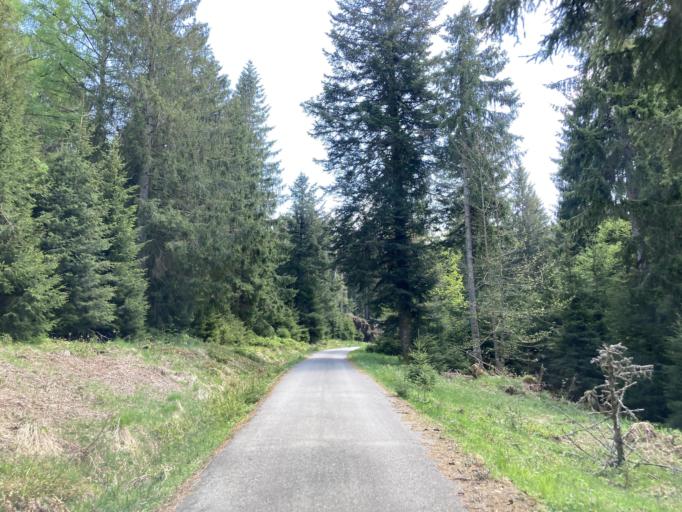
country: DE
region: Baden-Wuerttemberg
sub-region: Freiburg Region
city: Bad Peterstal-Griesbach
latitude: 48.5012
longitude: 8.2606
